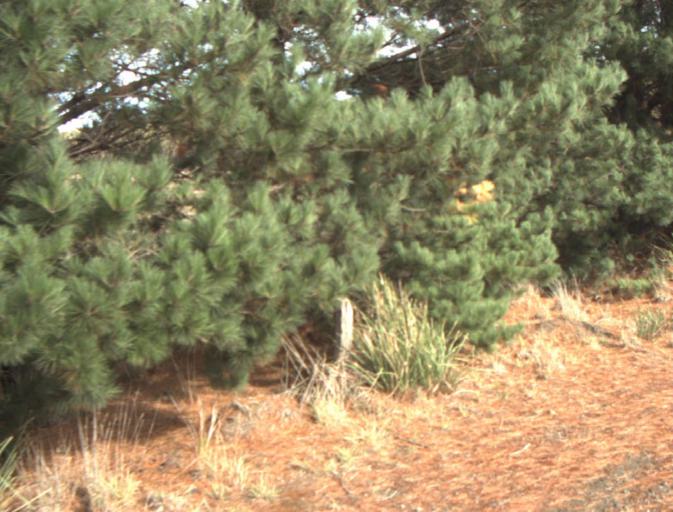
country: AU
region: Tasmania
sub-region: Launceston
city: Mayfield
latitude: -41.2100
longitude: 147.1849
